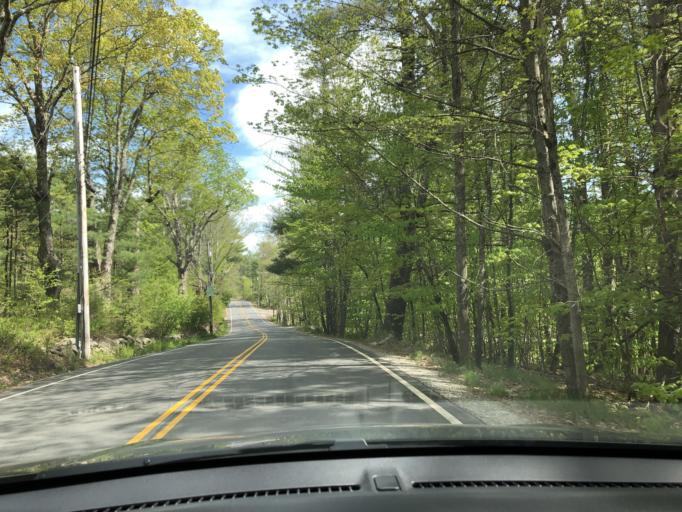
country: US
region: New Hampshire
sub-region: Merrimack County
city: New London
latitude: 43.4136
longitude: -72.0349
